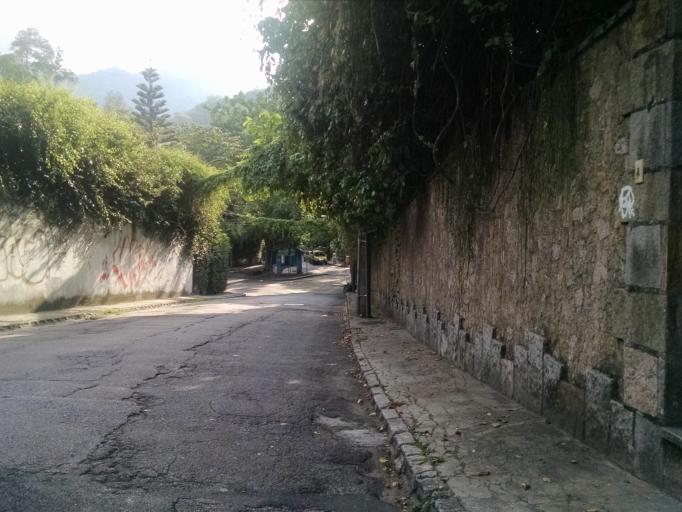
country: BR
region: Rio de Janeiro
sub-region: Rio De Janeiro
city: Rio de Janeiro
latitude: -22.9363
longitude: -43.1975
